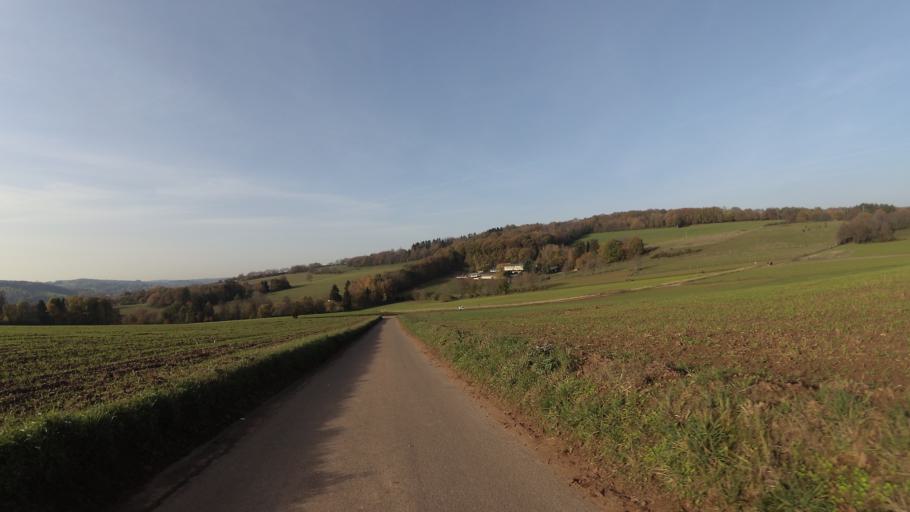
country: DE
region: Saarland
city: Hangard
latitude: 49.3905
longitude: 7.1964
